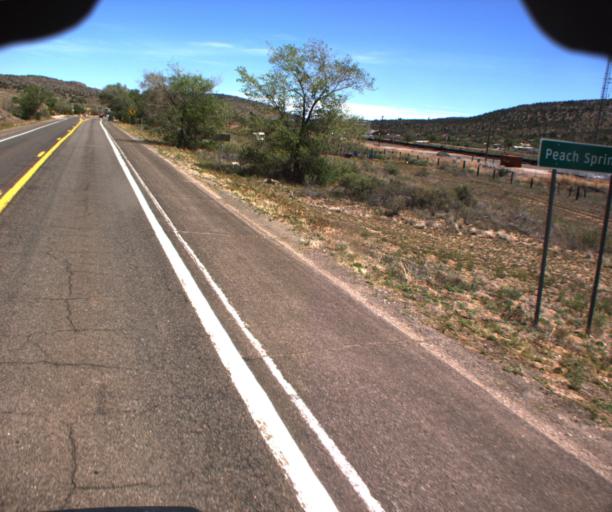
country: US
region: Arizona
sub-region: Mohave County
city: Peach Springs
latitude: 35.5275
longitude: -113.4318
